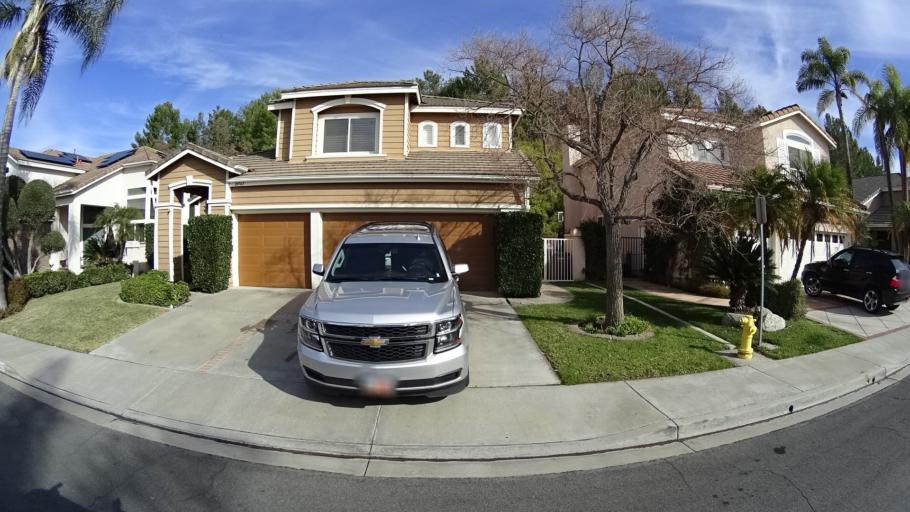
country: US
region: California
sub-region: Orange County
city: Portola Hills
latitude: 33.6769
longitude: -117.6323
